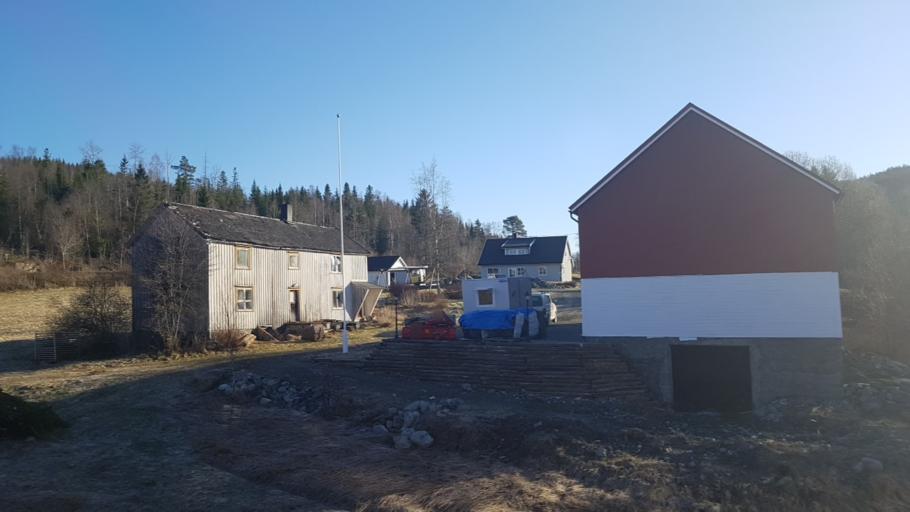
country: NO
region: Nord-Trondelag
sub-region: Levanger
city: Skogn
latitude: 63.6403
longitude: 11.0772
